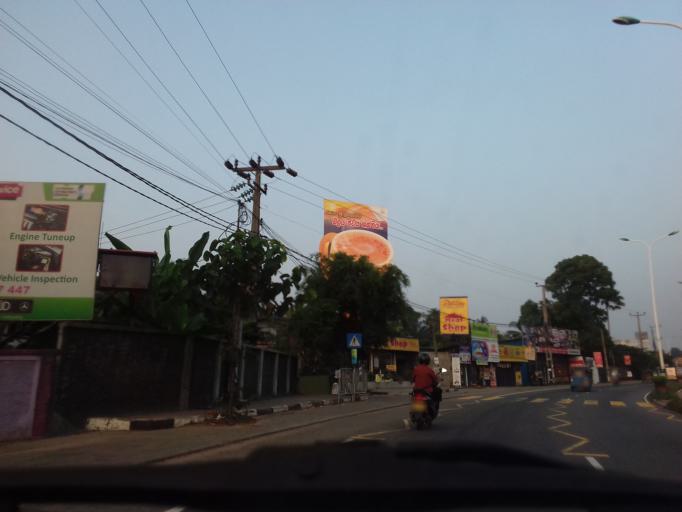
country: LK
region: Western
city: Kelaniya
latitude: 6.9921
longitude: 79.9418
